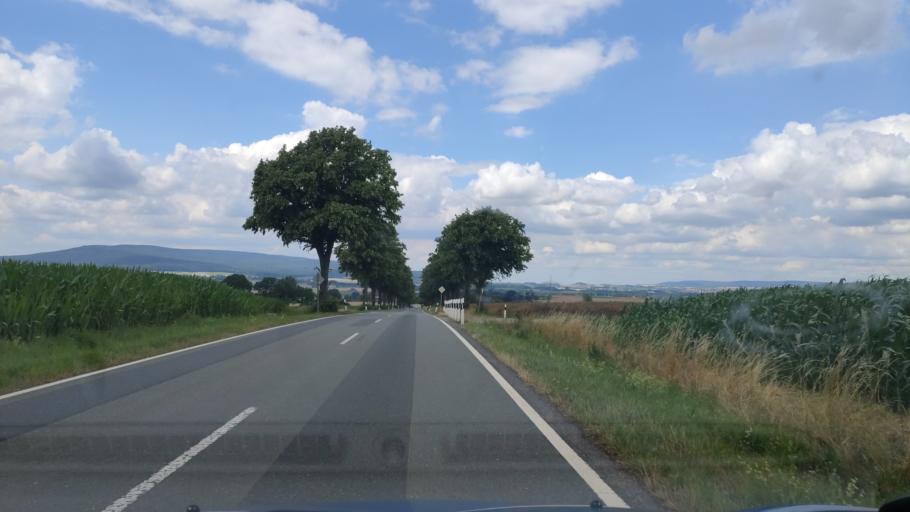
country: DE
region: Lower Saxony
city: Coppenbrugge
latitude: 52.1321
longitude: 9.4955
